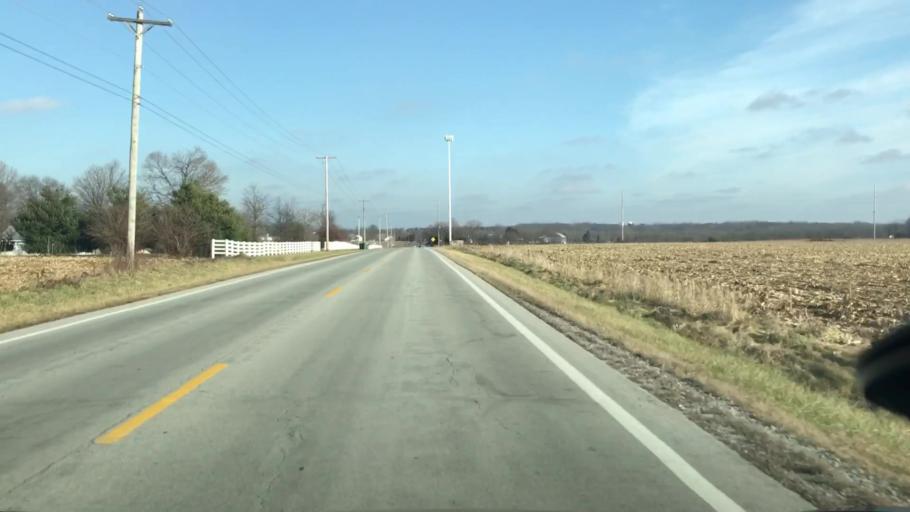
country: US
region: Ohio
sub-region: Greene County
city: Yellow Springs
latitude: 39.7947
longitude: -83.9387
